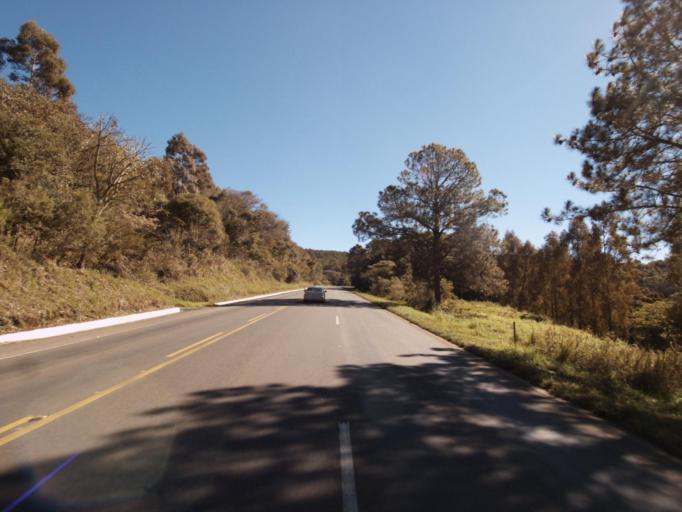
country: BR
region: Santa Catarina
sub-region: Joacaba
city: Joacaba
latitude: -26.9964
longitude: -51.7512
